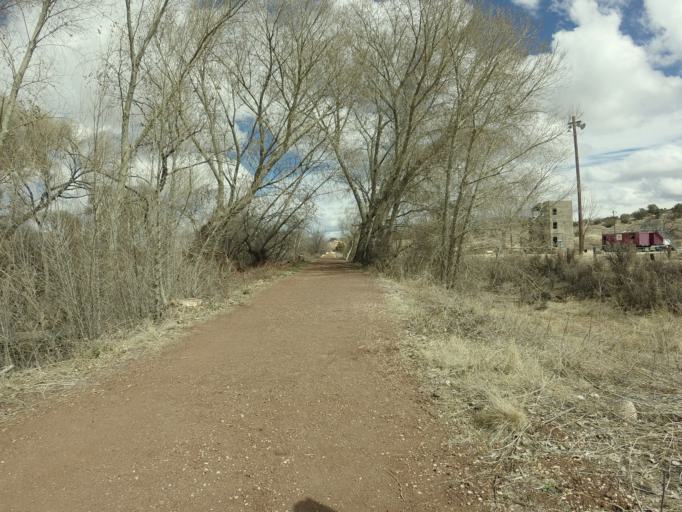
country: US
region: Arizona
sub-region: Yavapai County
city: Prescott
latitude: 34.5803
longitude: -112.4246
